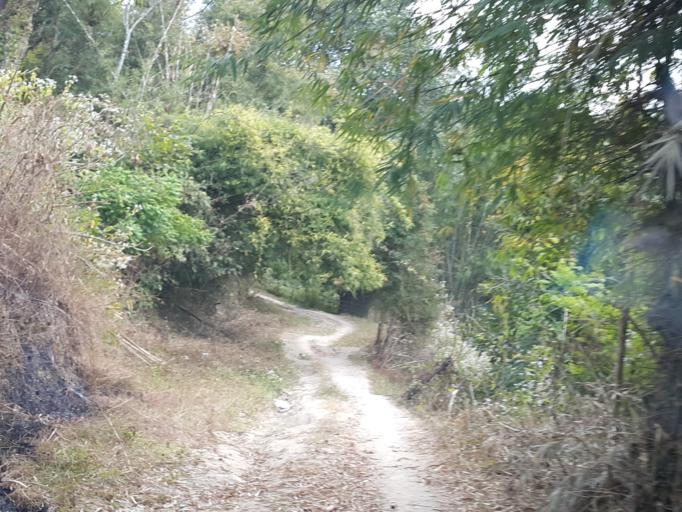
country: TH
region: Chiang Mai
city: Om Koi
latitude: 17.7989
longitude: 98.3341
